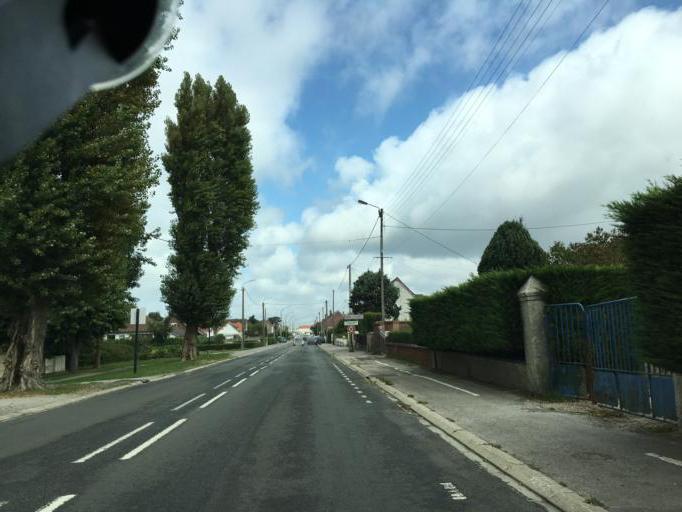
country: FR
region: Nord-Pas-de-Calais
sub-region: Departement du Pas-de-Calais
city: Rang-du-Fliers
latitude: 50.4119
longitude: 1.6476
